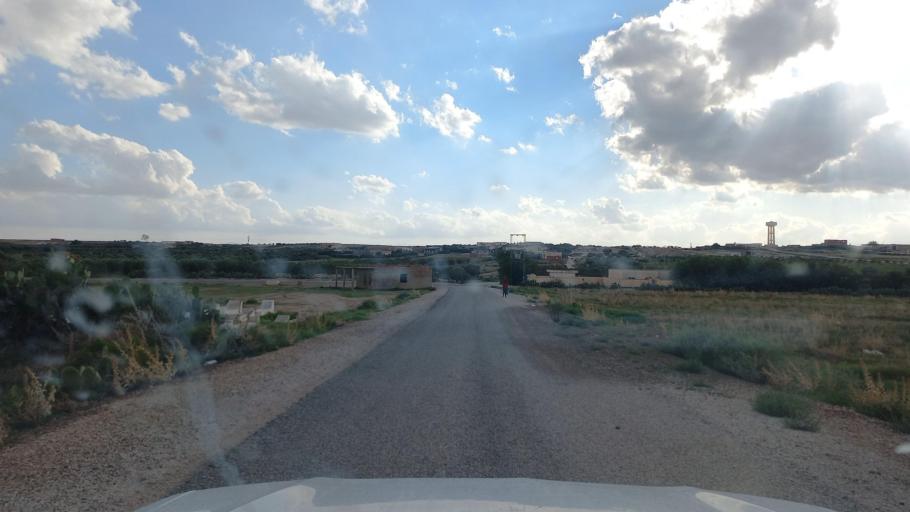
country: TN
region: Al Qasrayn
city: Sbiba
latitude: 35.3746
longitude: 9.0702
